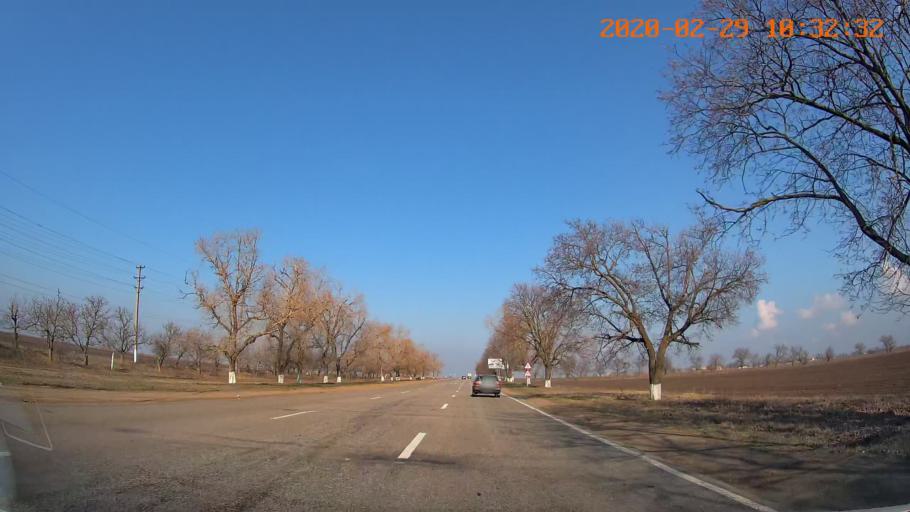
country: UA
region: Odessa
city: Velykoploske
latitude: 46.9620
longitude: 29.5532
